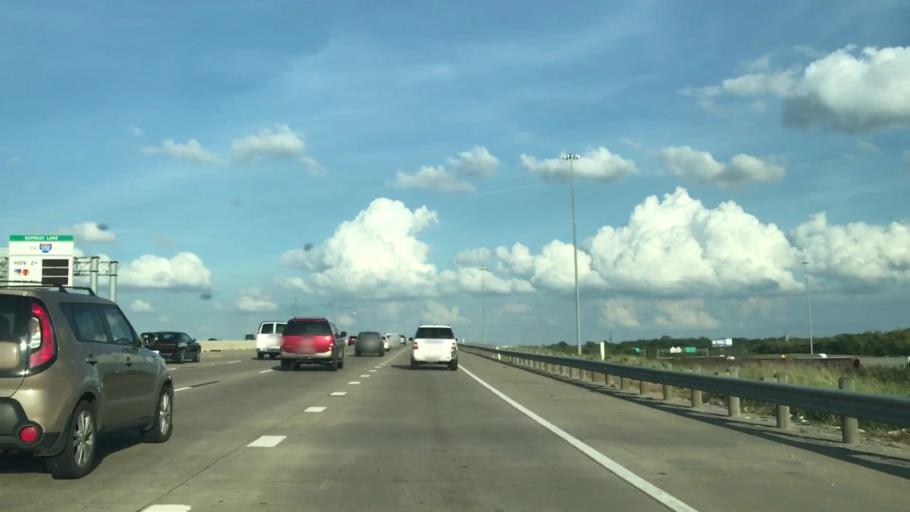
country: US
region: Texas
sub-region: Dallas County
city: Cockrell Hill
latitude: 32.7660
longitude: -96.9191
